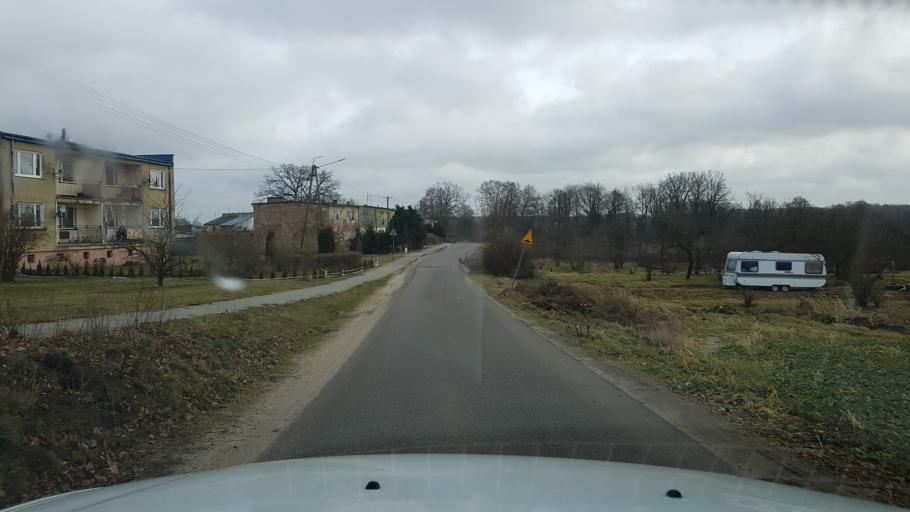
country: PL
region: West Pomeranian Voivodeship
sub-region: Powiat szczecinecki
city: Szczecinek
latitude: 53.7073
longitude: 16.7648
